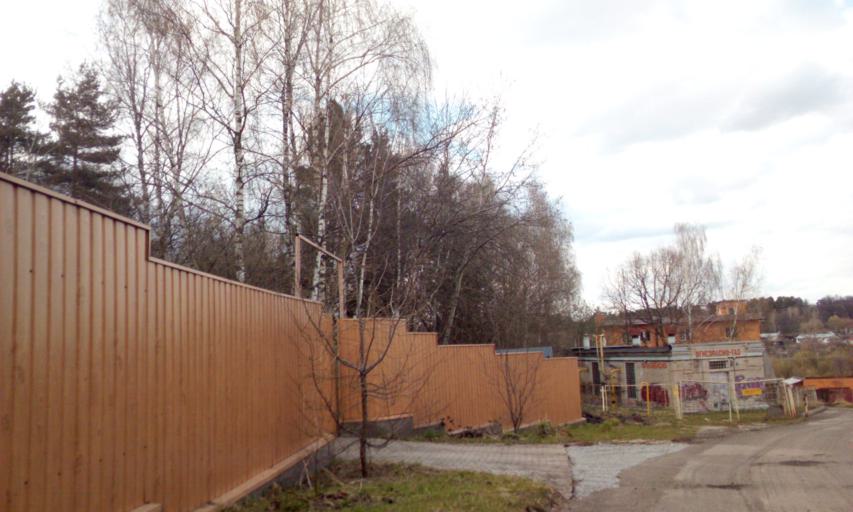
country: RU
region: Moscow
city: Tolstopal'tsevo
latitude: 55.6243
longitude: 37.2565
